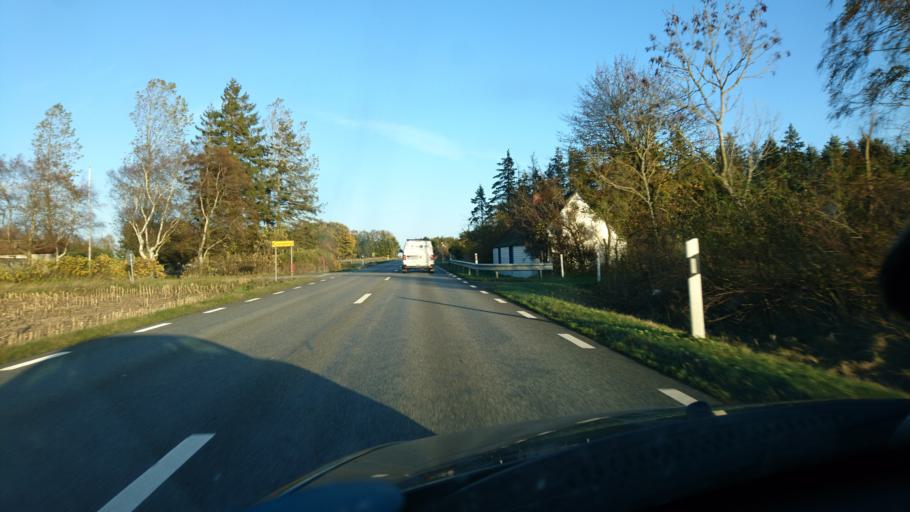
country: SE
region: Skane
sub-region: Tomelilla Kommun
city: Tomelilla
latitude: 55.5538
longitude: 14.0863
